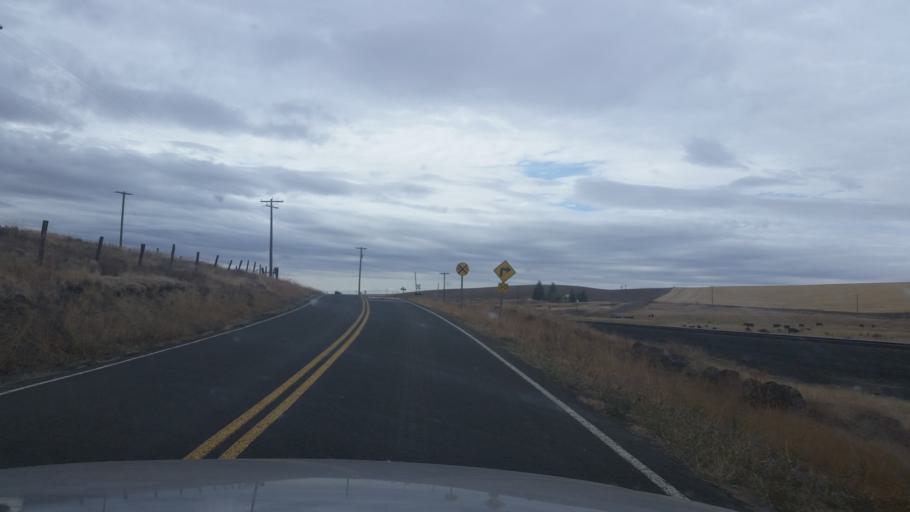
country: US
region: Washington
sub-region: Spokane County
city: Medical Lake
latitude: 47.5221
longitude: -117.9177
